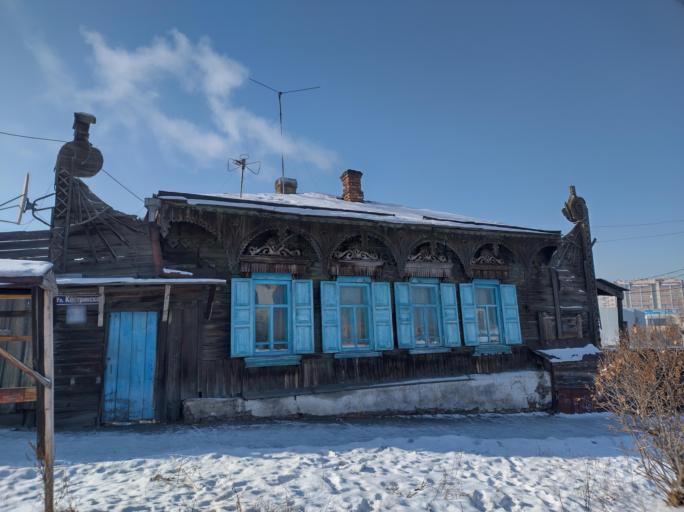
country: RU
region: Transbaikal Territory
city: Chita
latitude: 52.0389
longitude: 113.4883
